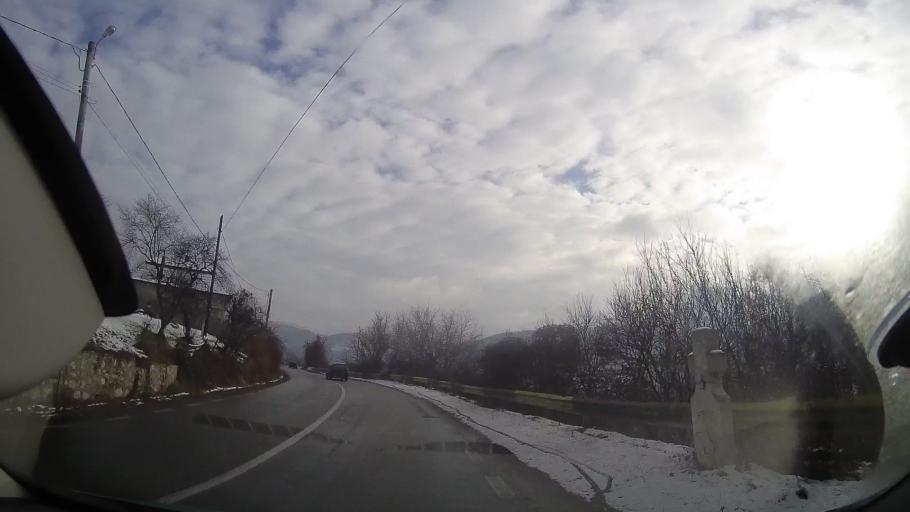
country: RO
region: Alba
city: Salciua de Sus
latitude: 46.3929
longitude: 23.3902
